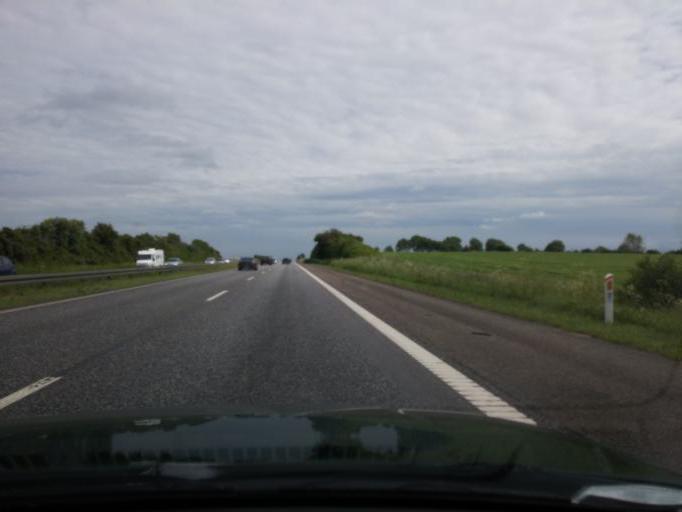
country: DK
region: South Denmark
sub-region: Middelfart Kommune
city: Ejby
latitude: 55.4581
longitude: 9.9311
